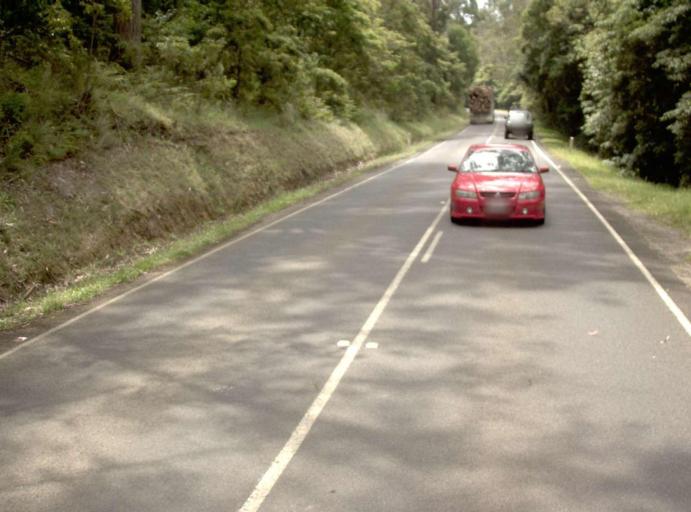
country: AU
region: Victoria
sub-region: Latrobe
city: Traralgon
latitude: -38.4319
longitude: 146.7377
